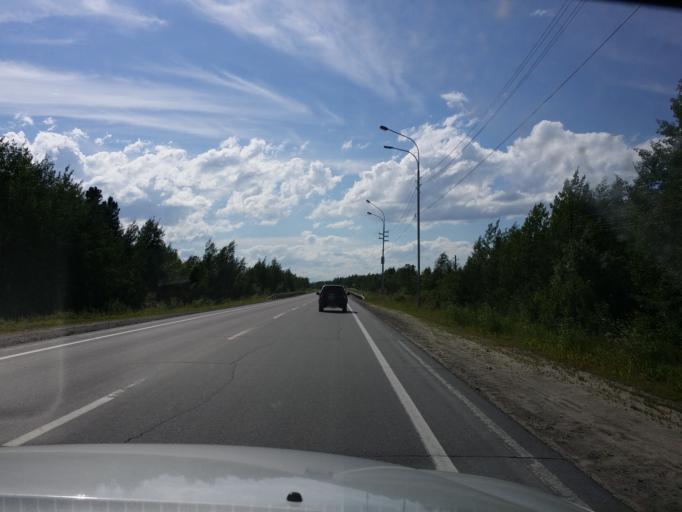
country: RU
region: Khanty-Mansiyskiy Avtonomnyy Okrug
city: Izluchinsk
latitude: 60.9651
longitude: 76.7834
